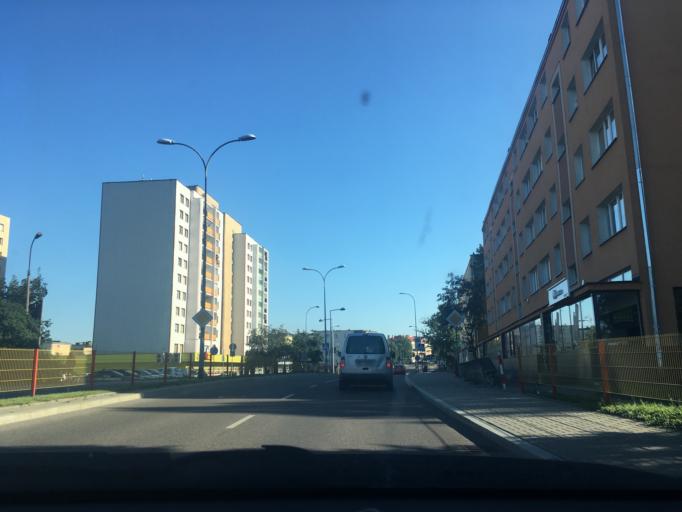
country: PL
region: Podlasie
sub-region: Bialystok
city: Bialystok
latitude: 53.1378
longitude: 23.1518
